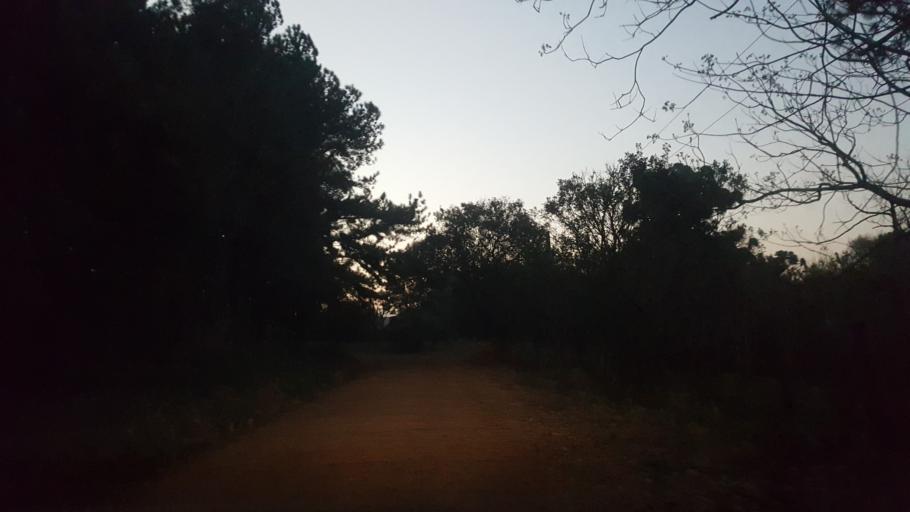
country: AR
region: Misiones
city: Capiovi
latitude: -26.9001
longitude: -55.0550
